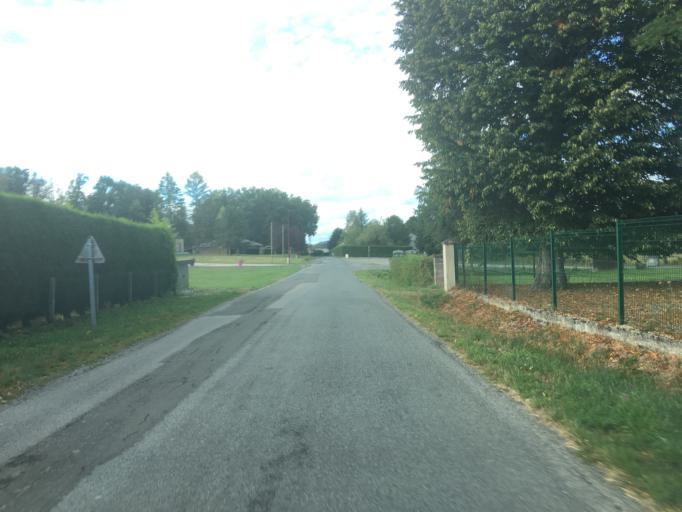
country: FR
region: Limousin
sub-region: Departement de la Correze
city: Bort-les-Orgues
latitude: 45.4162
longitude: 2.4392
